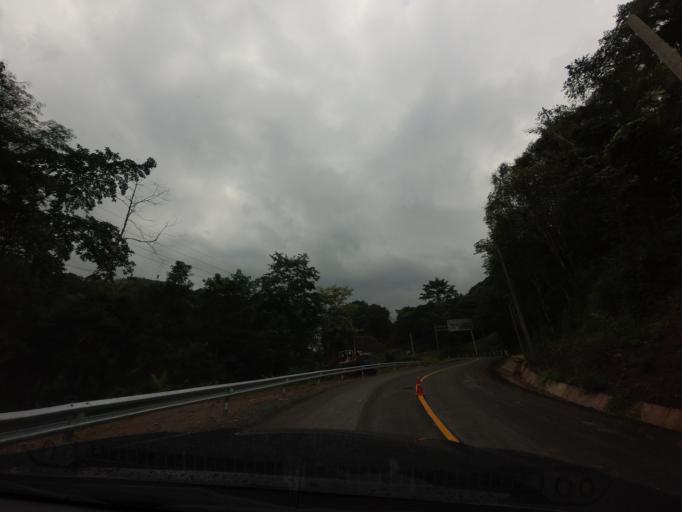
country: TH
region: Nan
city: Bo Kluea
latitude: 19.1824
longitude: 101.1772
